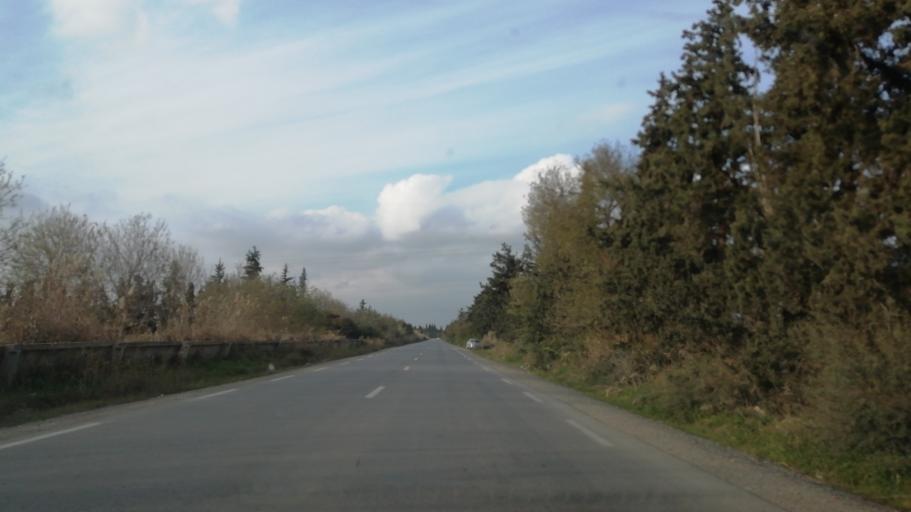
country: DZ
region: Mascara
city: Mascara
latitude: 35.6259
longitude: 0.0432
